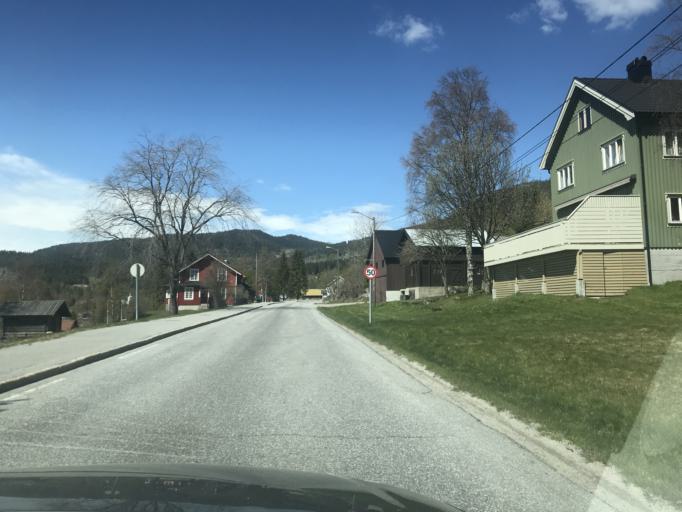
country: NO
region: Telemark
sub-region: Hjartdal
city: Sauland
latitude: 59.7513
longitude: 8.7982
